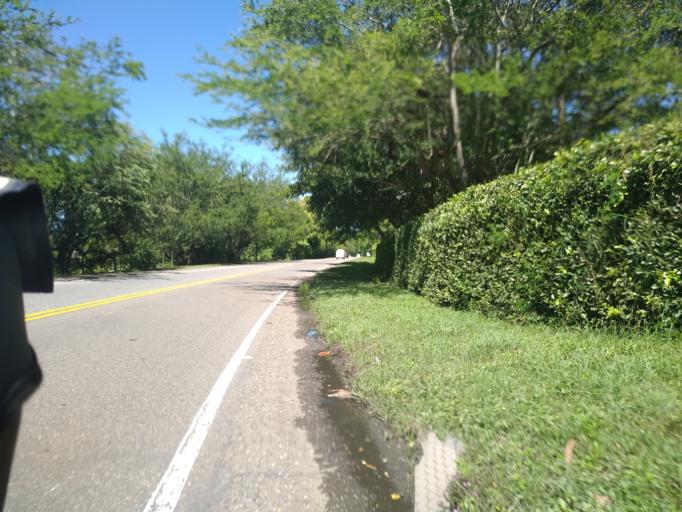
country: CO
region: Caldas
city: La Dorada
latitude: 5.4244
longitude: -74.6830
